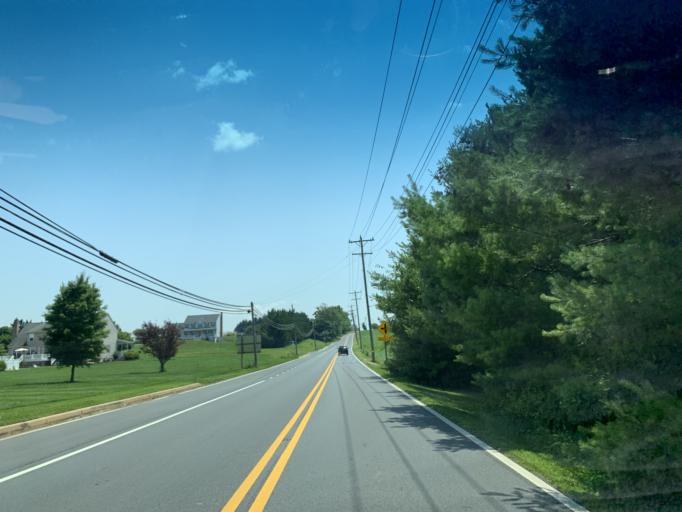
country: US
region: Maryland
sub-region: Frederick County
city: Green Valley
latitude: 39.3557
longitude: -77.2698
